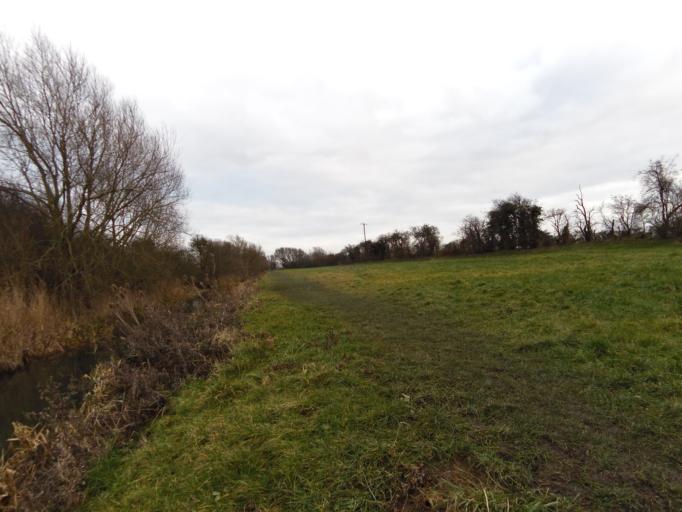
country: GB
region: England
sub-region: Cambridgeshire
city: Waterbeach
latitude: 52.2655
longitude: 0.2176
